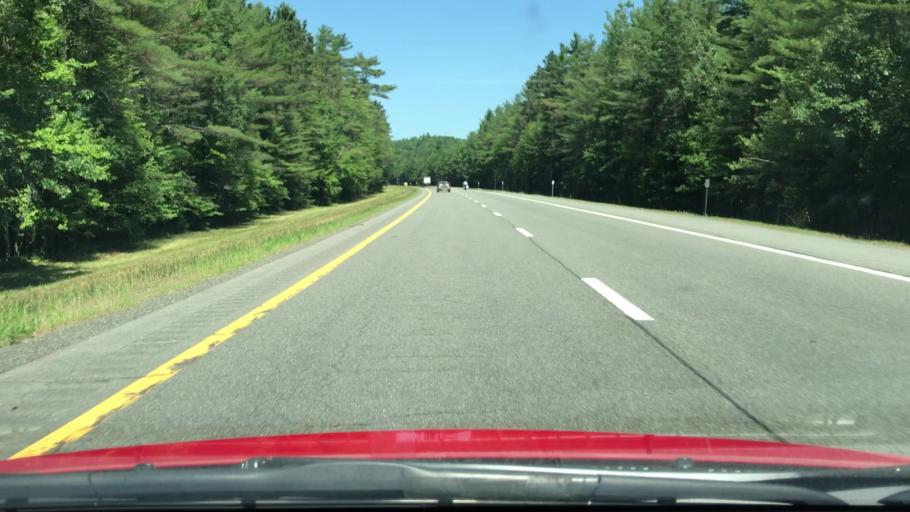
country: US
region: New York
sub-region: Essex County
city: Elizabethtown
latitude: 44.3171
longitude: -73.5280
